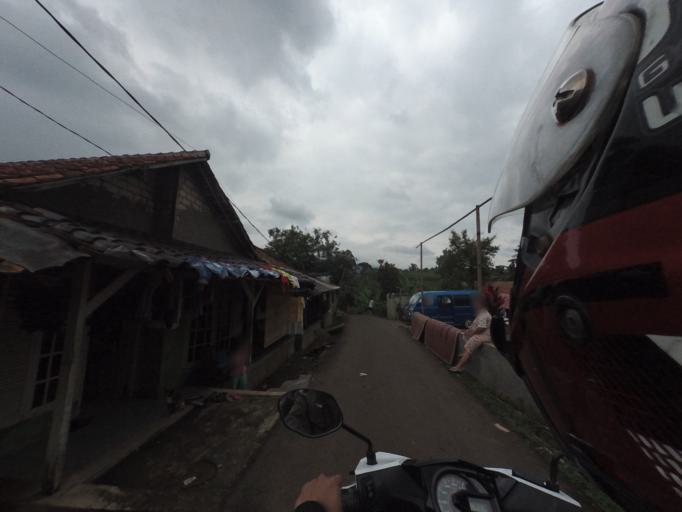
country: ID
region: West Java
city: Bogor
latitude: -6.6130
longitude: 106.7380
